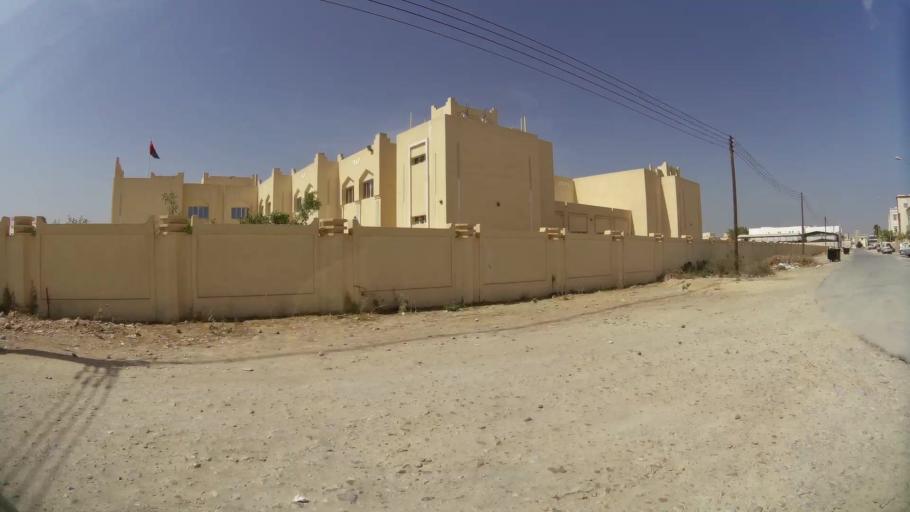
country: OM
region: Zufar
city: Salalah
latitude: 17.0442
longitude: 54.1551
